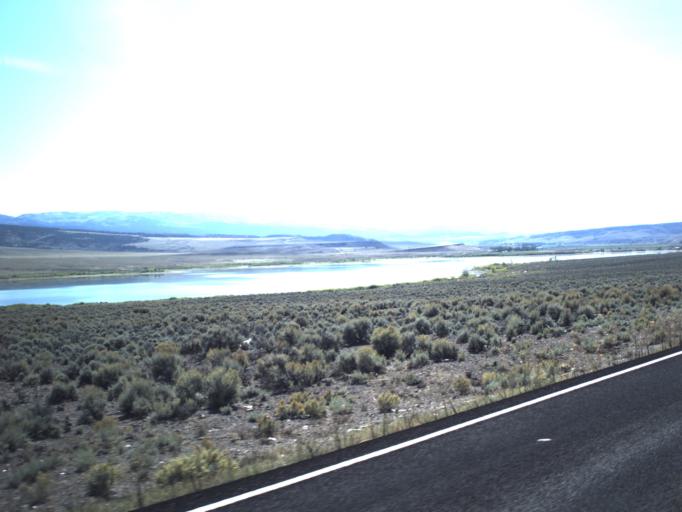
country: US
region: Utah
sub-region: Piute County
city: Junction
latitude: 38.1926
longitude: -112.0115
